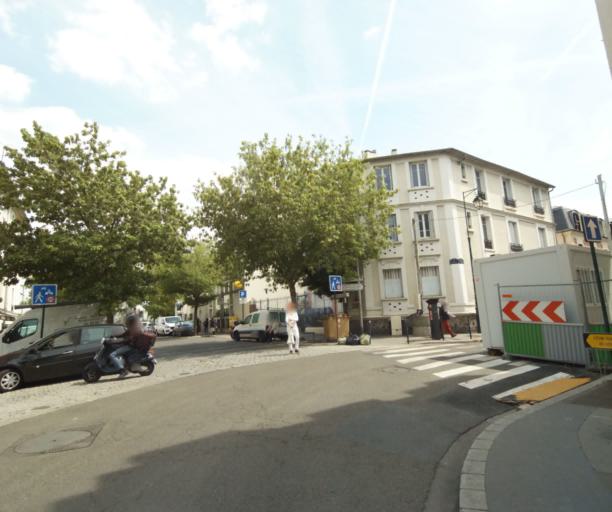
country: FR
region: Ile-de-France
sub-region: Departement des Hauts-de-Seine
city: Colombes
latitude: 48.9230
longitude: 2.2589
